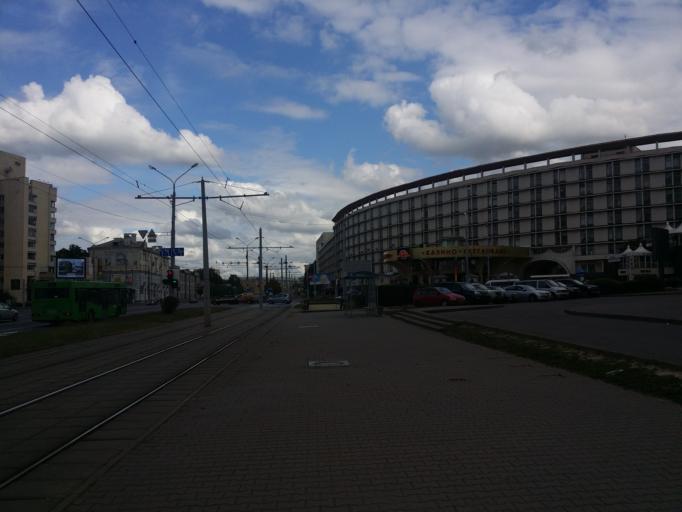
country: BY
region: Minsk
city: Minsk
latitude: 53.9167
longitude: 27.5625
